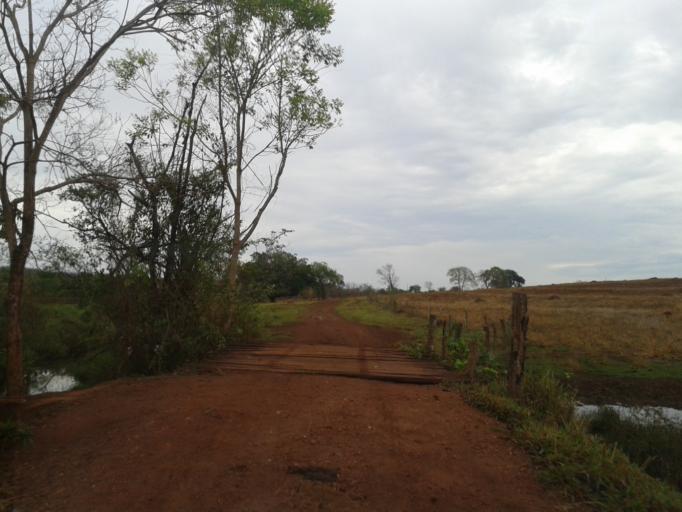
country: BR
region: Minas Gerais
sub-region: Santa Vitoria
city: Santa Vitoria
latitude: -18.8640
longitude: -49.8250
